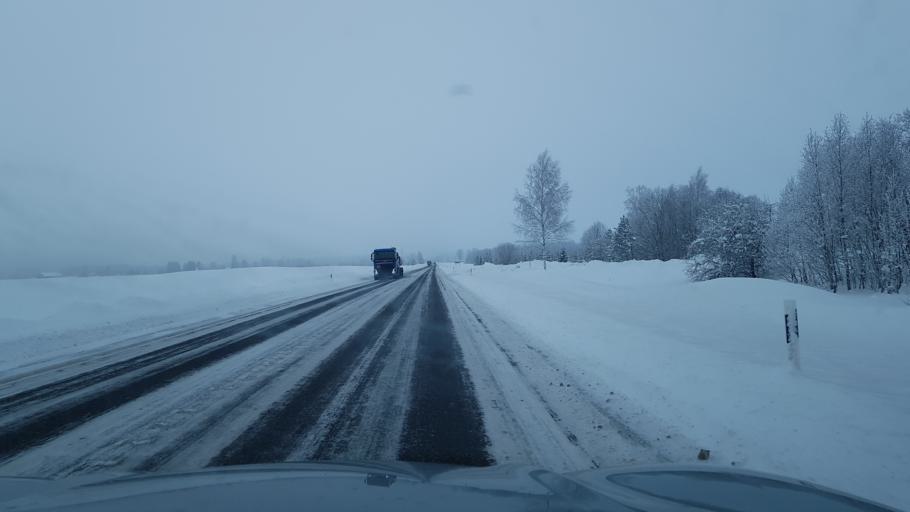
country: EE
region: Ida-Virumaa
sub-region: Johvi vald
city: Johvi
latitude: 59.2476
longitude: 27.3703
